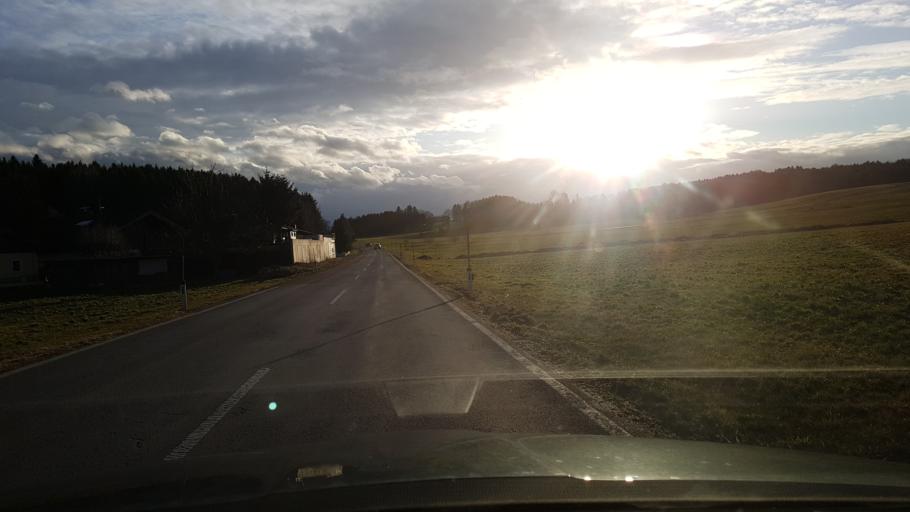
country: AT
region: Salzburg
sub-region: Politischer Bezirk Salzburg-Umgebung
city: Schleedorf
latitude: 47.9411
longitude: 13.1708
